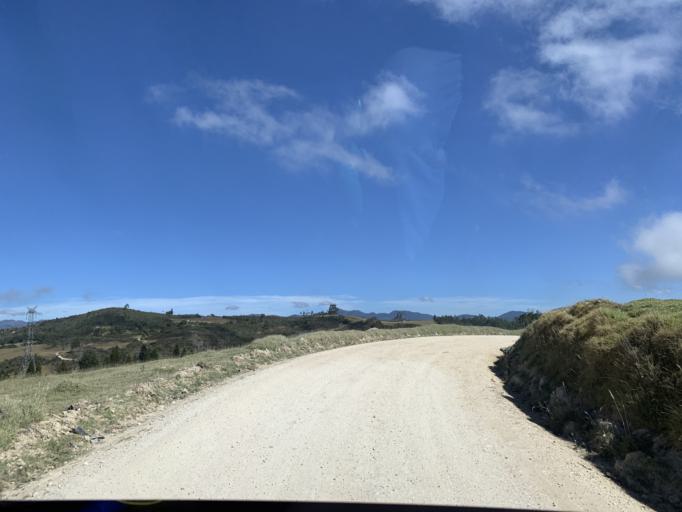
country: CO
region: Boyaca
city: Tuta
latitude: 5.6899
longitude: -73.1460
